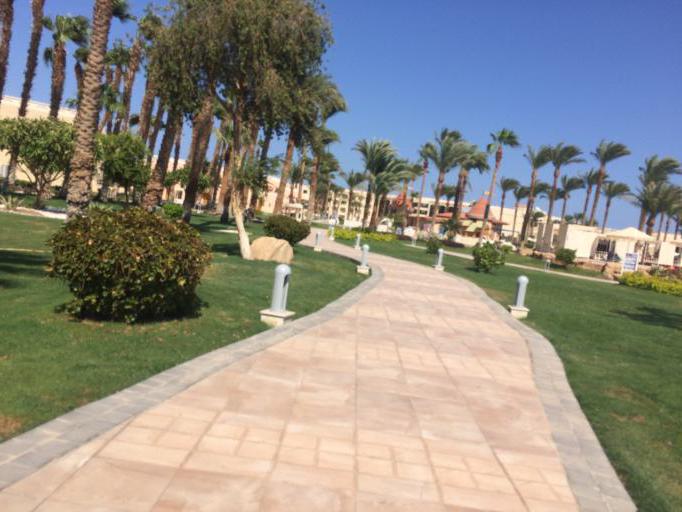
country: EG
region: Red Sea
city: Hurghada
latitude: 27.1224
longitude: 33.8258
